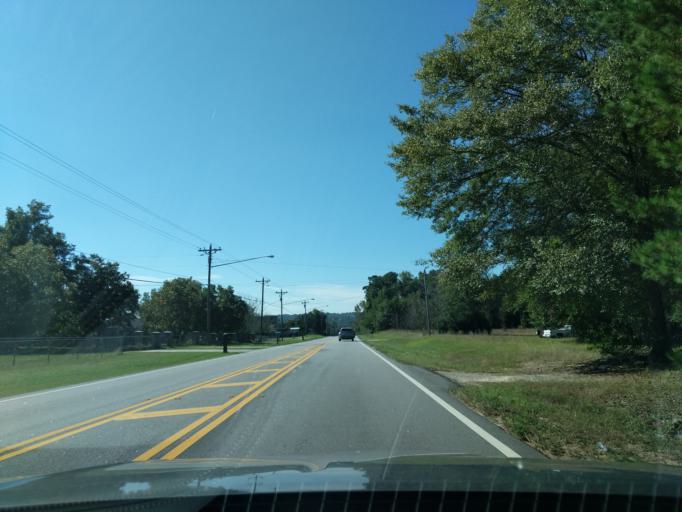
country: US
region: Georgia
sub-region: Richmond County
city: Hephzibah
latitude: 33.3535
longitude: -81.9998
